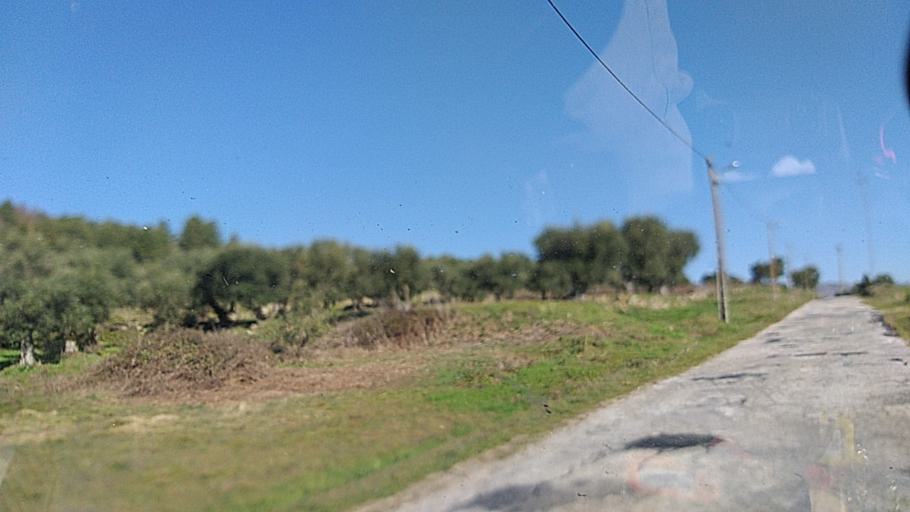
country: PT
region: Guarda
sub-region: Celorico da Beira
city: Celorico da Beira
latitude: 40.6892
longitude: -7.4541
